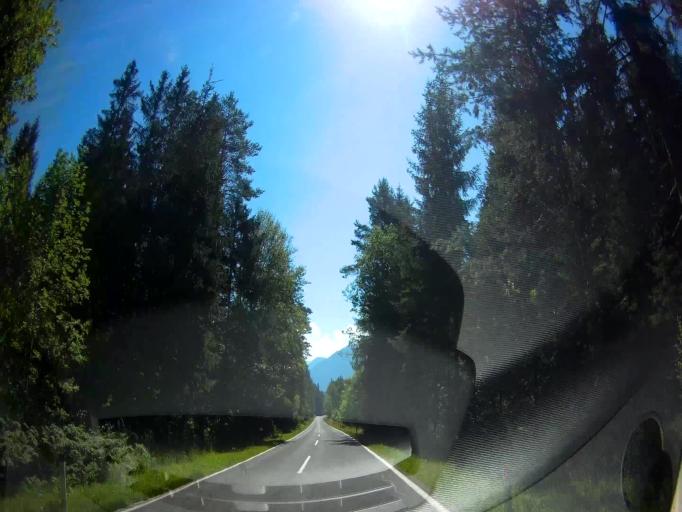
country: AT
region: Carinthia
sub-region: Politischer Bezirk Volkermarkt
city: Gallizien
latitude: 46.5426
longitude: 14.5459
